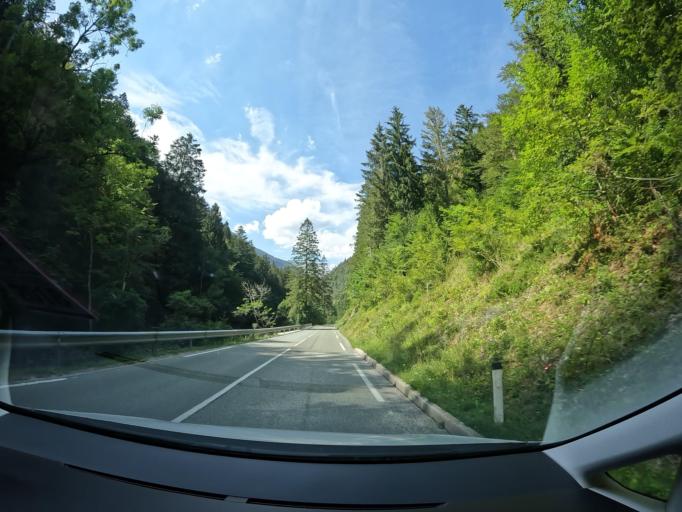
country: SI
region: Jezersko
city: Zgornje Jezersko
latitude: 46.3517
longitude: 14.4735
